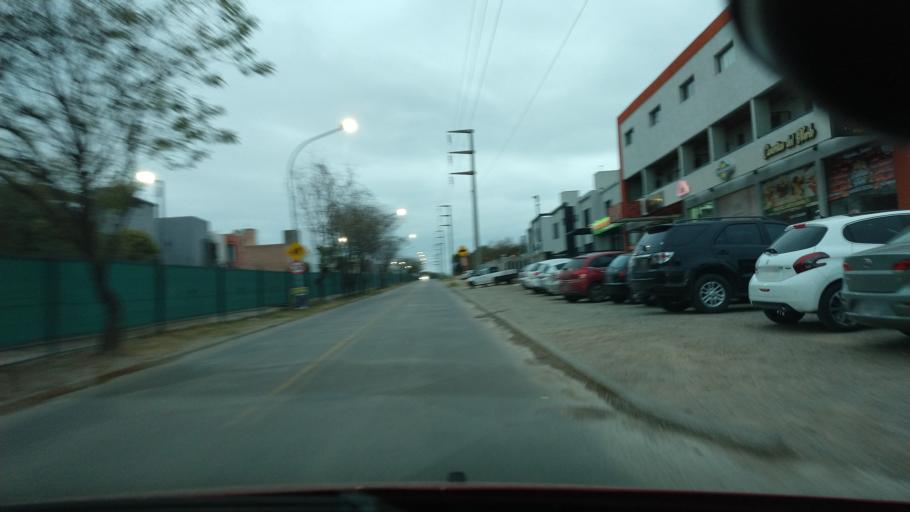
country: AR
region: Cordoba
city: La Calera
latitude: -31.3785
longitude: -64.2721
